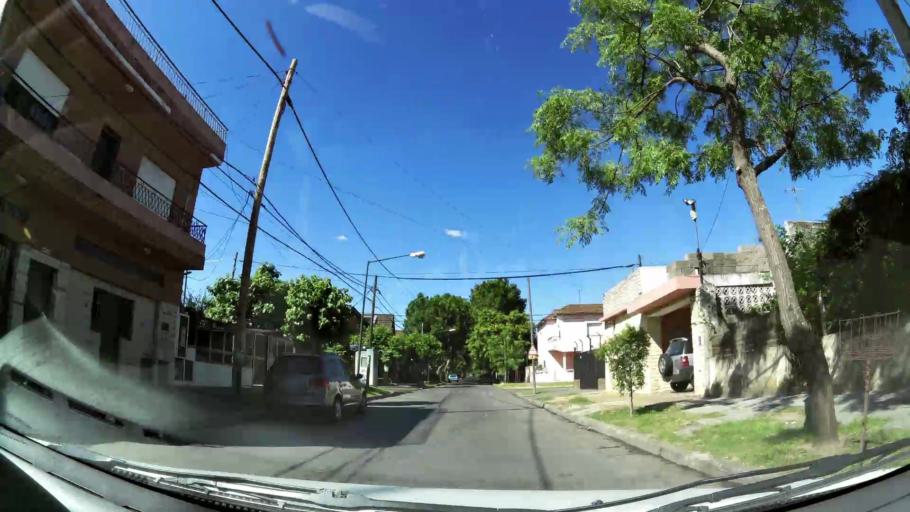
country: AR
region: Buenos Aires
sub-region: Partido de San Isidro
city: San Isidro
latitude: -34.5106
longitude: -58.5744
